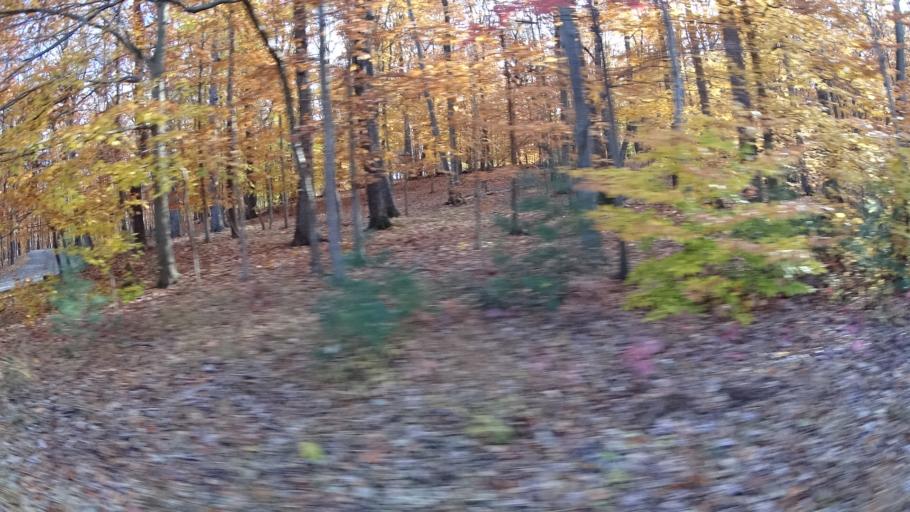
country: US
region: New Jersey
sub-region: Somerset County
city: Bernardsville
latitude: 40.7555
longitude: -74.5318
